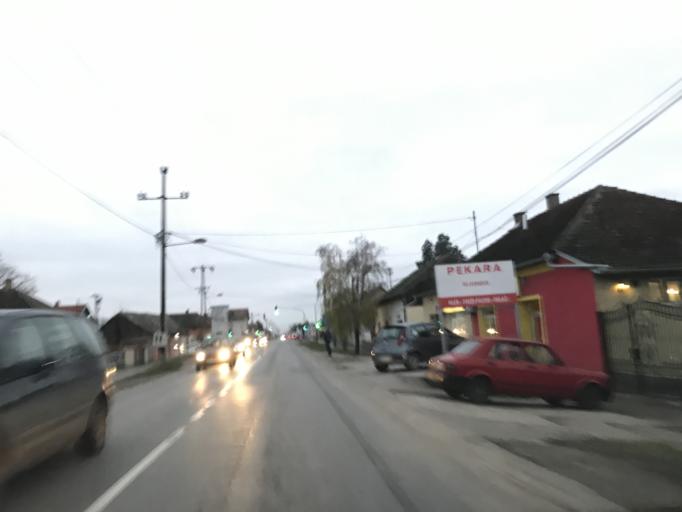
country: RS
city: Rumenka
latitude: 45.2922
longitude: 19.7429
